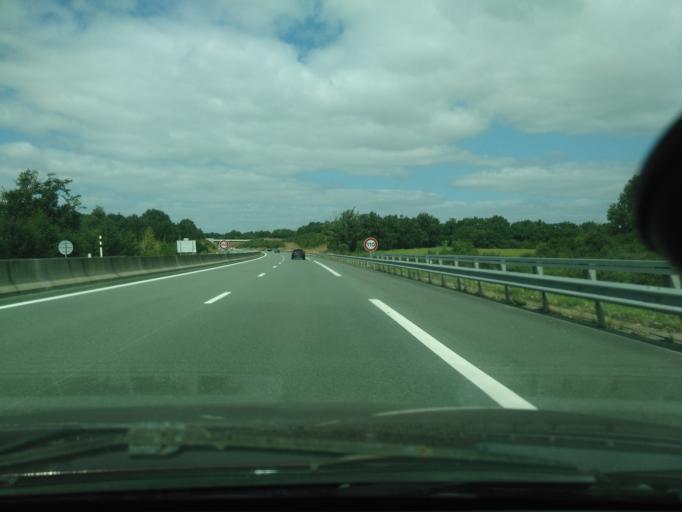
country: FR
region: Pays de la Loire
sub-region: Departement de la Vendee
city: Les Clouzeaux
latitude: 46.6414
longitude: -1.5029
